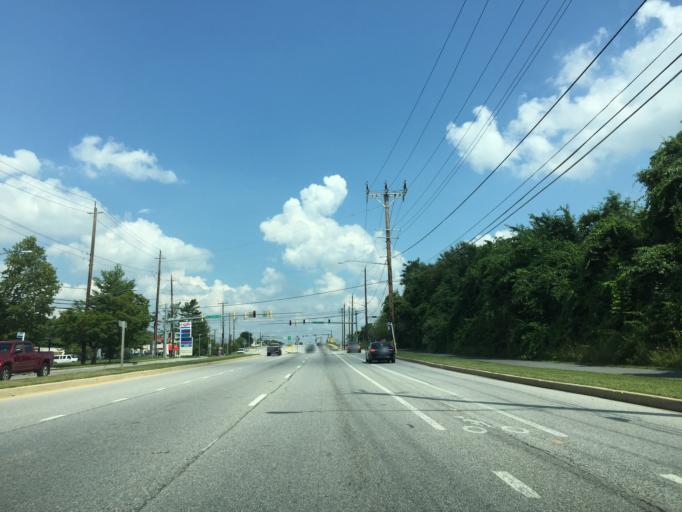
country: US
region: Maryland
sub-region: Montgomery County
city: Fairland
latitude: 39.0637
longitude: -76.9672
